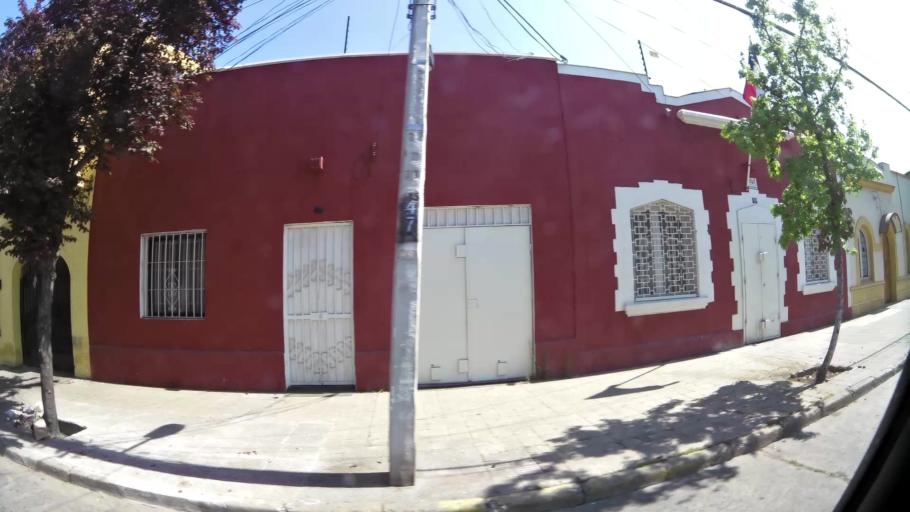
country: CL
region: Santiago Metropolitan
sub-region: Provincia de Santiago
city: Santiago
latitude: -33.4632
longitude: -70.6328
